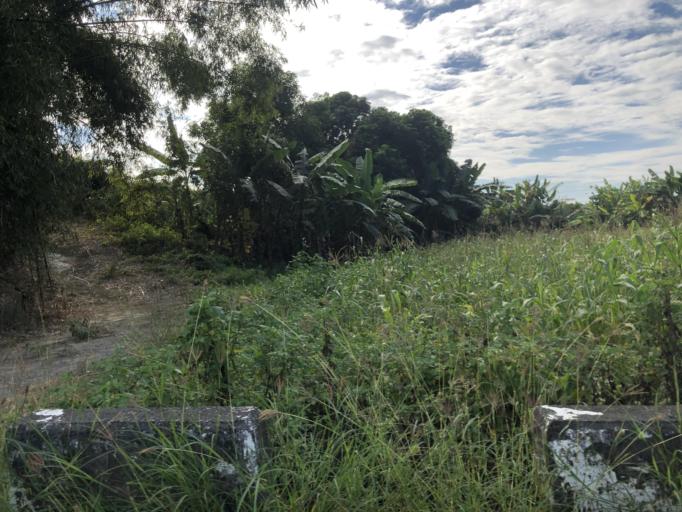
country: TW
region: Taiwan
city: Yujing
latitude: 23.0419
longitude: 120.4233
